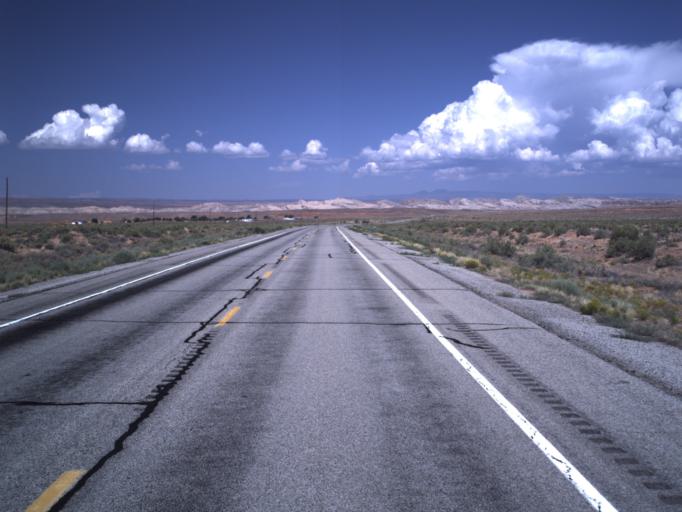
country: US
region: Utah
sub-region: San Juan County
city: Blanding
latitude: 37.2004
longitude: -109.6036
